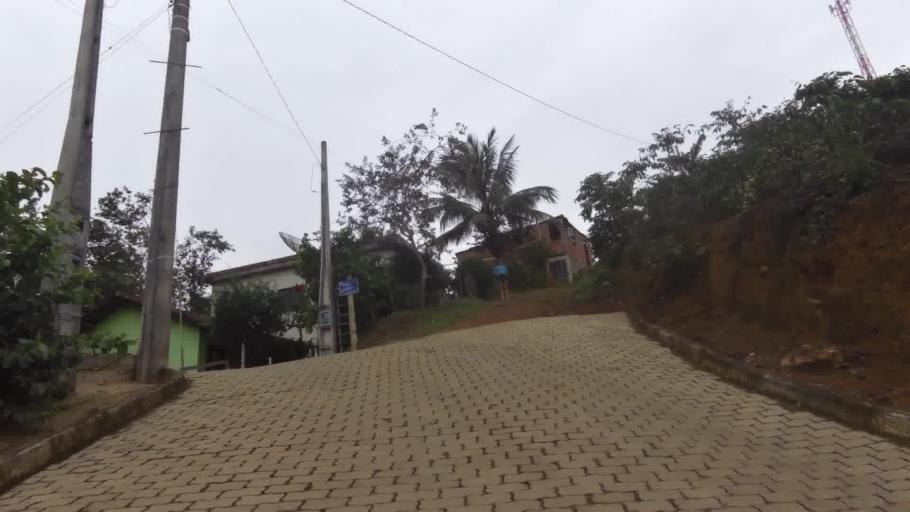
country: BR
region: Espirito Santo
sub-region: Iconha
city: Iconha
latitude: -20.7903
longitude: -40.8181
